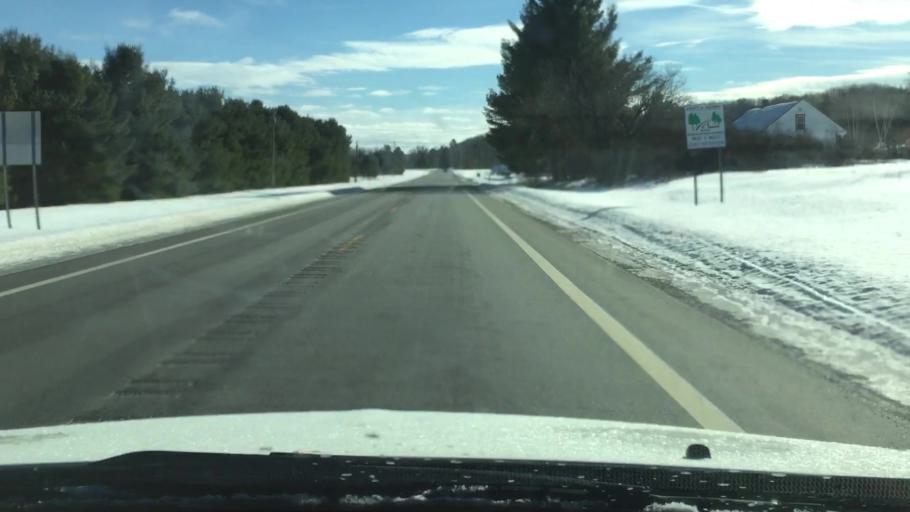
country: US
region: Michigan
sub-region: Charlevoix County
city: East Jordan
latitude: 45.0730
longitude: -85.0864
